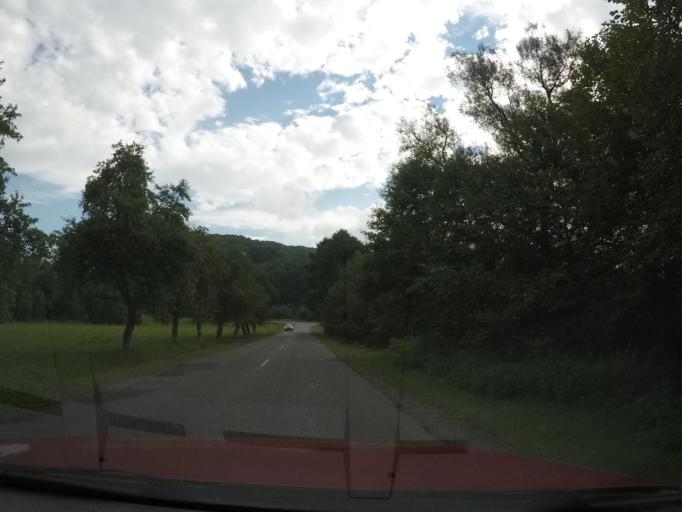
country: UA
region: Zakarpattia
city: Velykyi Bereznyi
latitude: 48.9523
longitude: 22.5452
